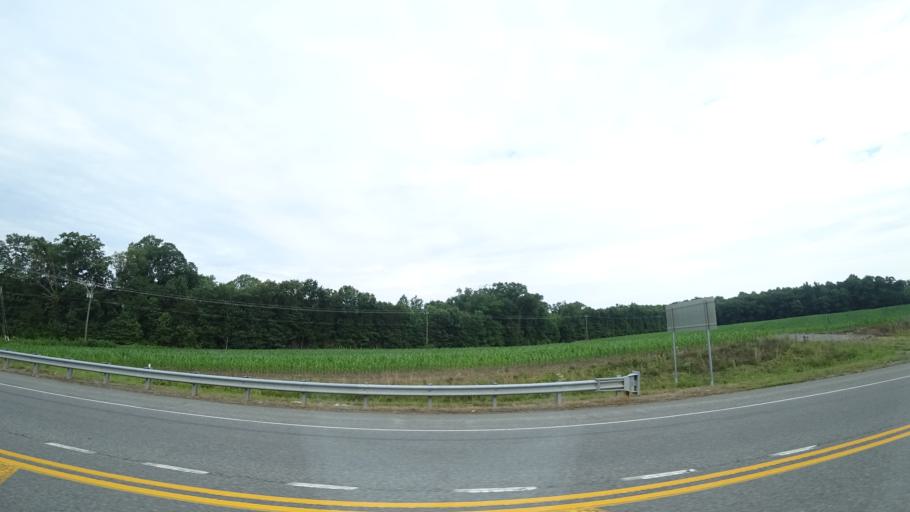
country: US
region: Virginia
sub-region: Spotsylvania County
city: Spotsylvania Courthouse
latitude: 38.1634
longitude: -77.6411
